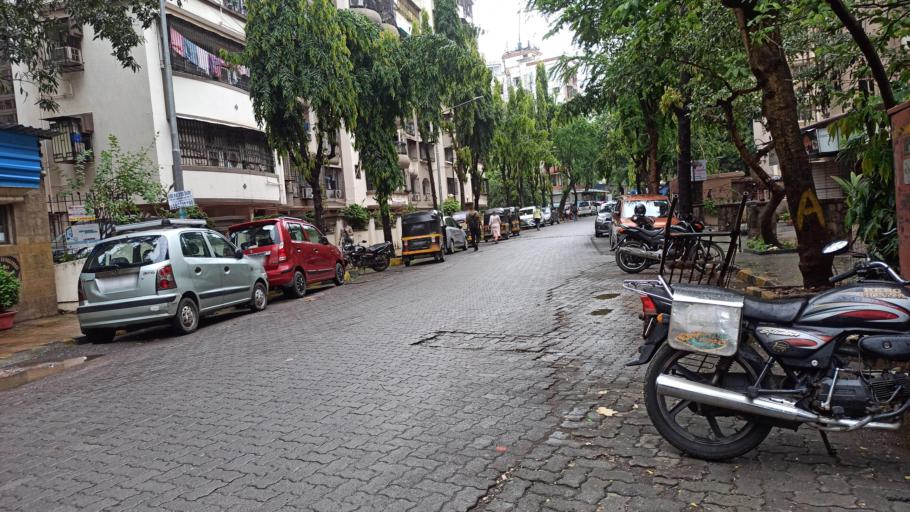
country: IN
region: Maharashtra
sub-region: Mumbai Suburban
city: Borivli
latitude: 19.2599
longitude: 72.8516
